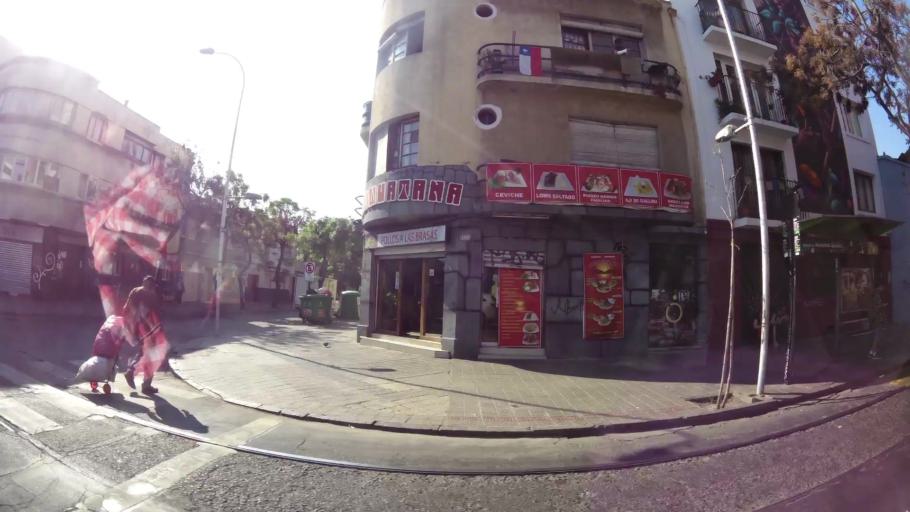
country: CL
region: Santiago Metropolitan
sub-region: Provincia de Santiago
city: Santiago
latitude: -33.4386
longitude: -70.6623
